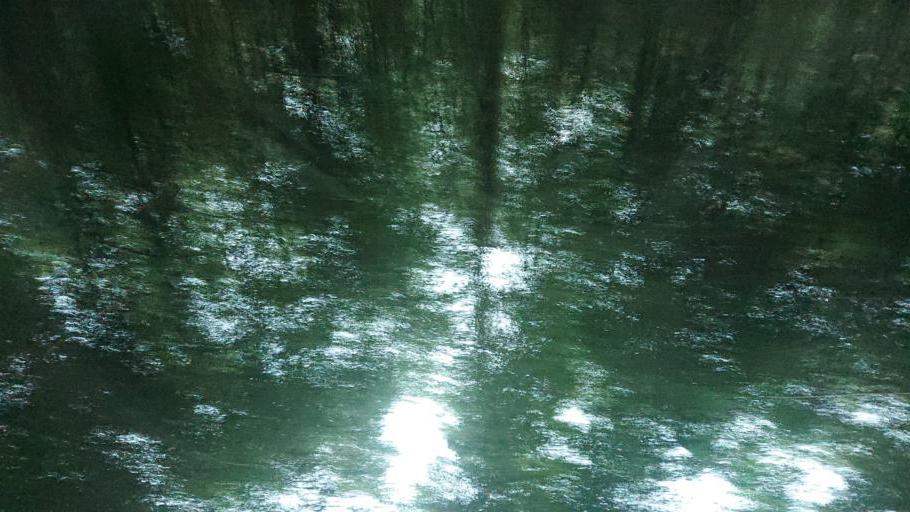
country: TW
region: Taiwan
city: Lugu
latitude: 23.5842
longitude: 120.7247
